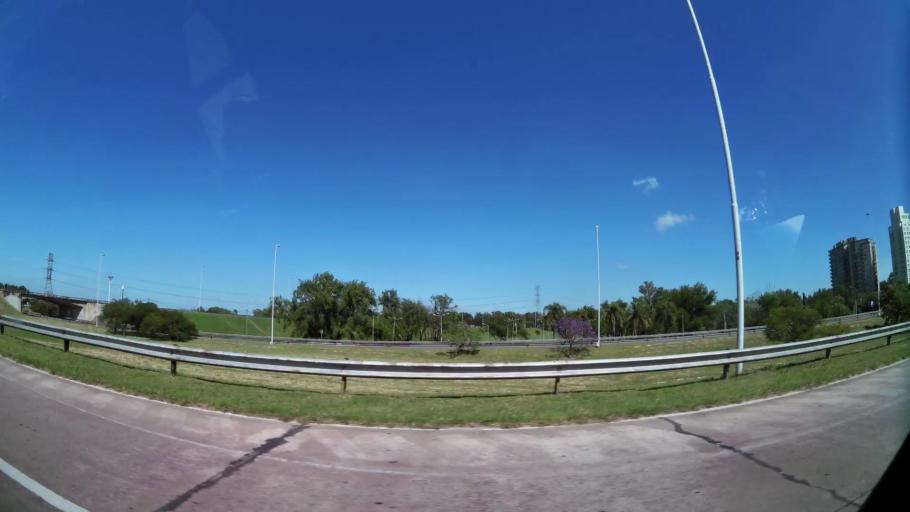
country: AR
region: Buenos Aires
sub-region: Partido de Tigre
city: Tigre
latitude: -34.4347
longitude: -58.5852
